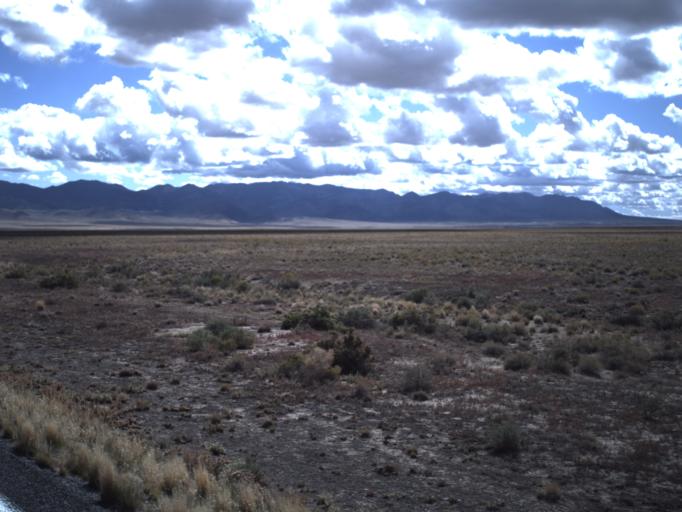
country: US
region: Utah
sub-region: Beaver County
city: Milford
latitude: 38.5452
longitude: -113.7167
